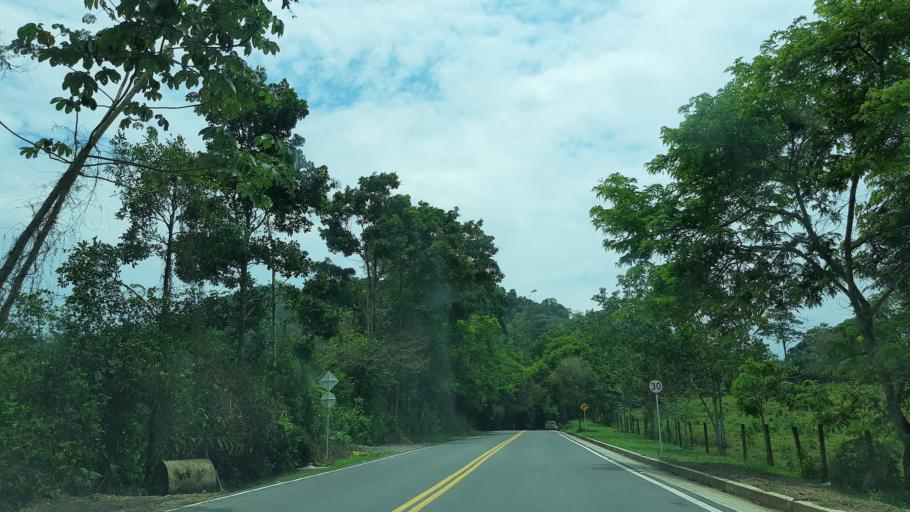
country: CO
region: Boyaca
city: San Luis de Gaceno
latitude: 4.8342
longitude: -73.1230
